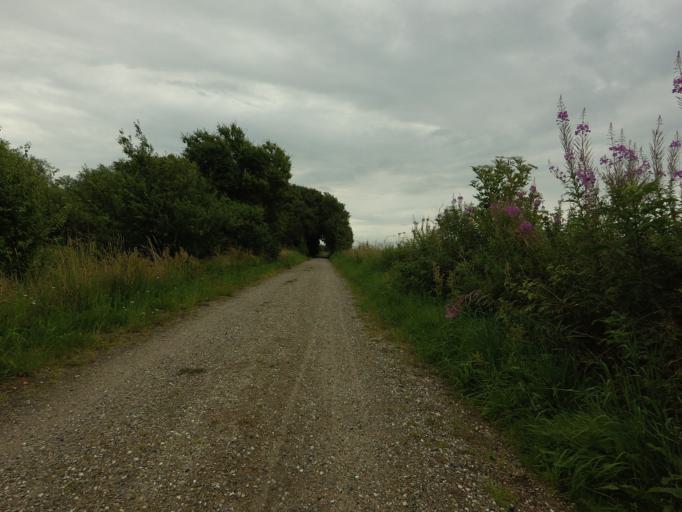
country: DK
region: North Denmark
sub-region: Alborg Kommune
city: Vadum
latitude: 57.1112
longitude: 9.8839
